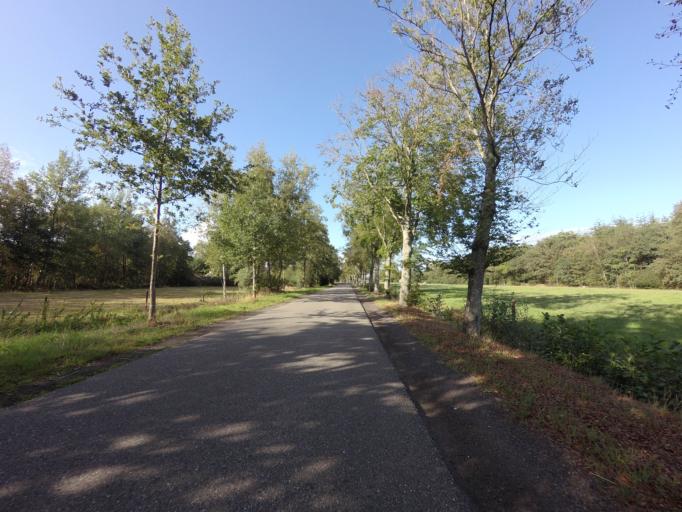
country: NL
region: Friesland
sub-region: Gemeente Heerenveen
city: Jubbega
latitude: 53.0049
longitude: 6.2320
